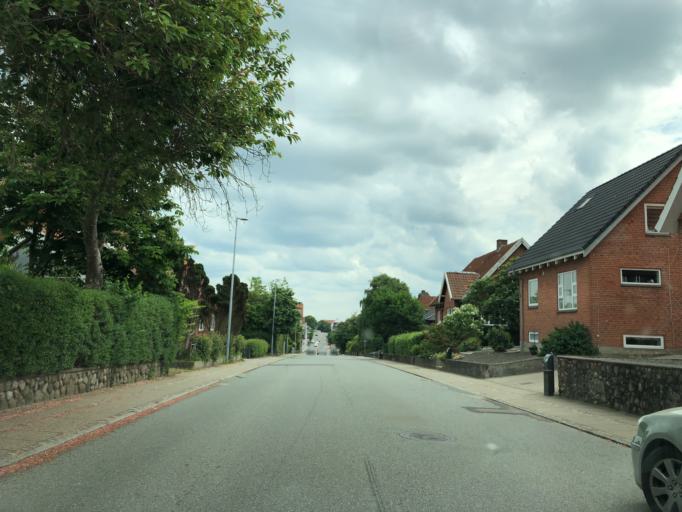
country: DK
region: Central Jutland
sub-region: Struer Kommune
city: Struer
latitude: 56.4911
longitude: 8.5799
